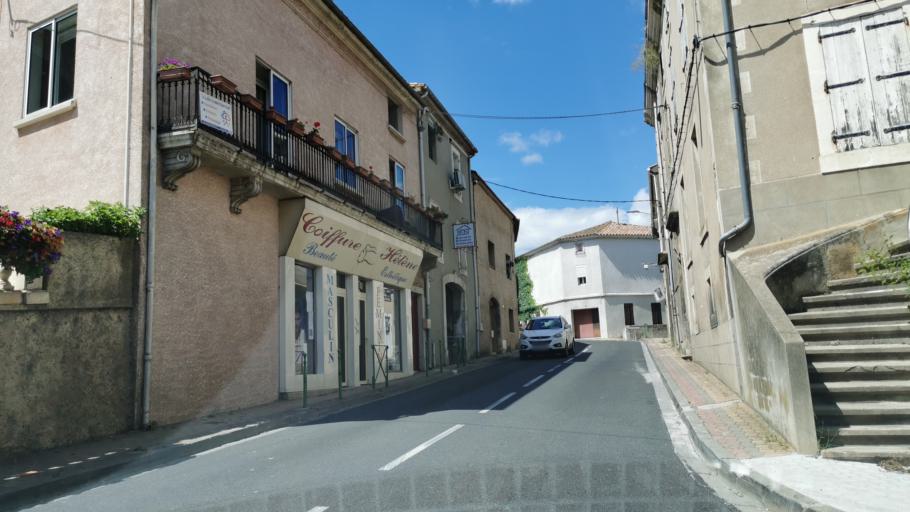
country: FR
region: Languedoc-Roussillon
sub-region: Departement de l'Aude
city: Saint-Marcel-sur-Aude
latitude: 43.2421
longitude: 2.9238
